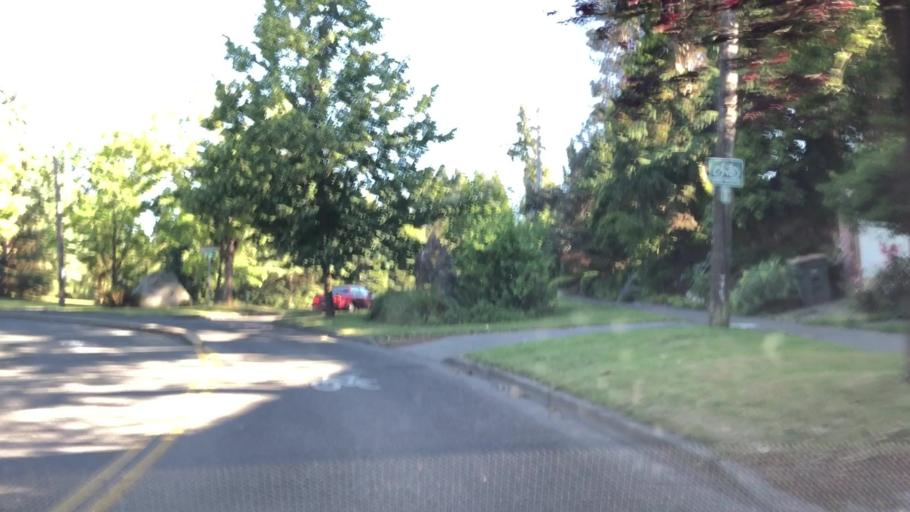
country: US
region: Washington
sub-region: King County
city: Seattle
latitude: 47.6415
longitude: -122.2987
